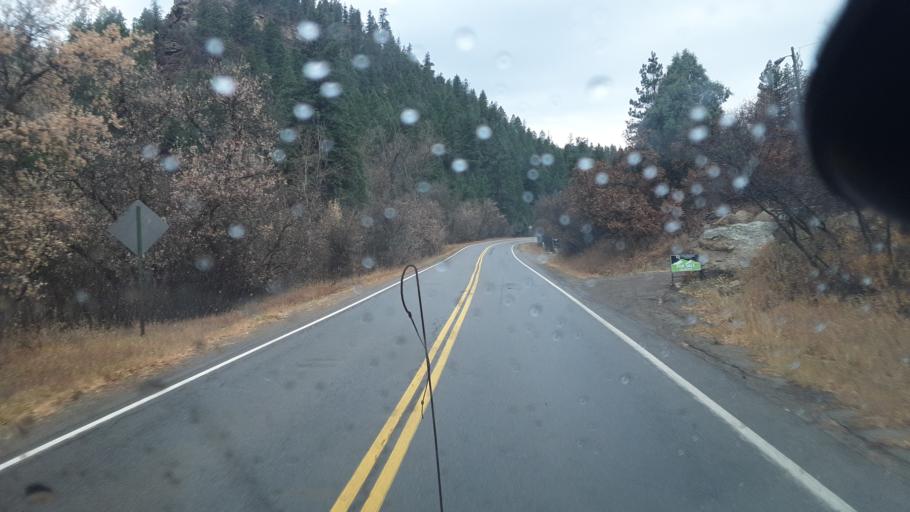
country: US
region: Colorado
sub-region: La Plata County
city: Durango
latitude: 37.2599
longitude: -107.9249
